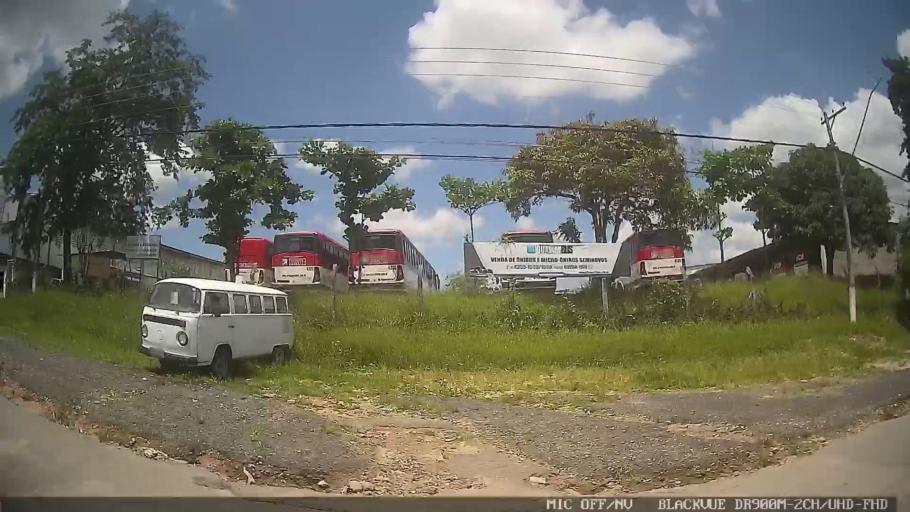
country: BR
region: Sao Paulo
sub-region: Jacarei
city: Jacarei
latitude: -23.3090
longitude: -46.0032
